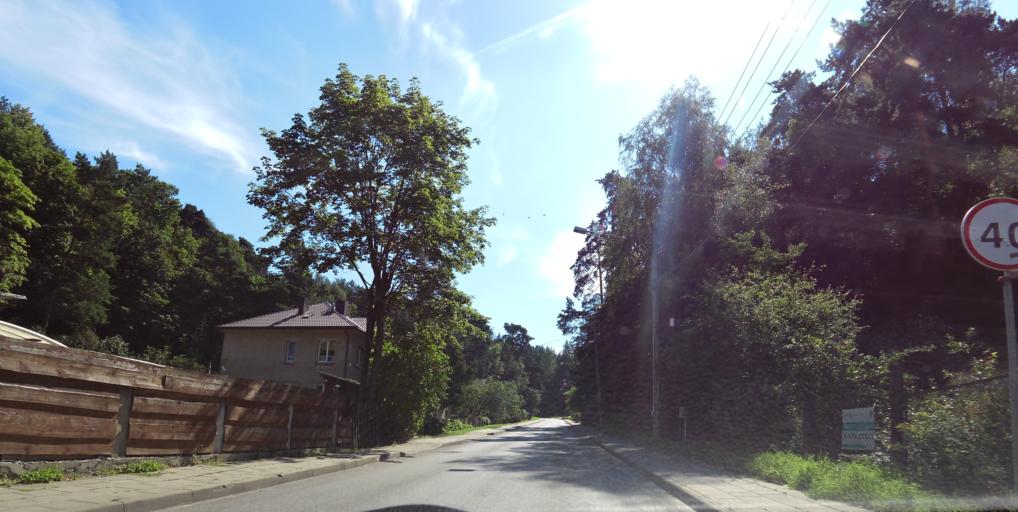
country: LT
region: Vilnius County
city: Rasos
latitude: 54.6912
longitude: 25.3152
